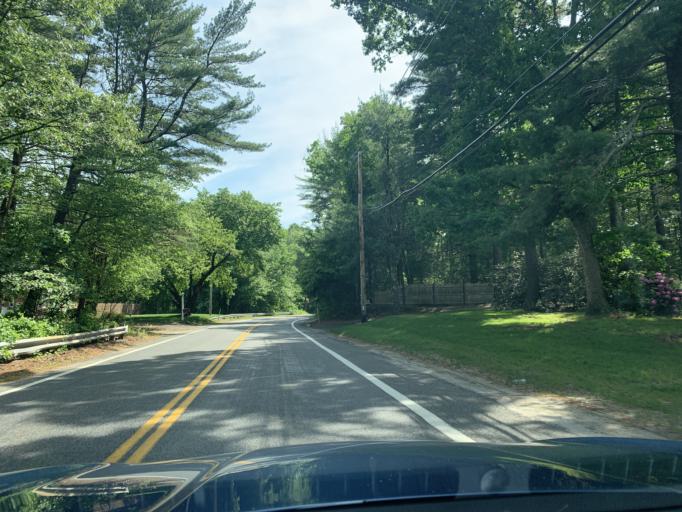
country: US
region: Rhode Island
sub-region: Kent County
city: West Greenwich
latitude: 41.6660
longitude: -71.6157
